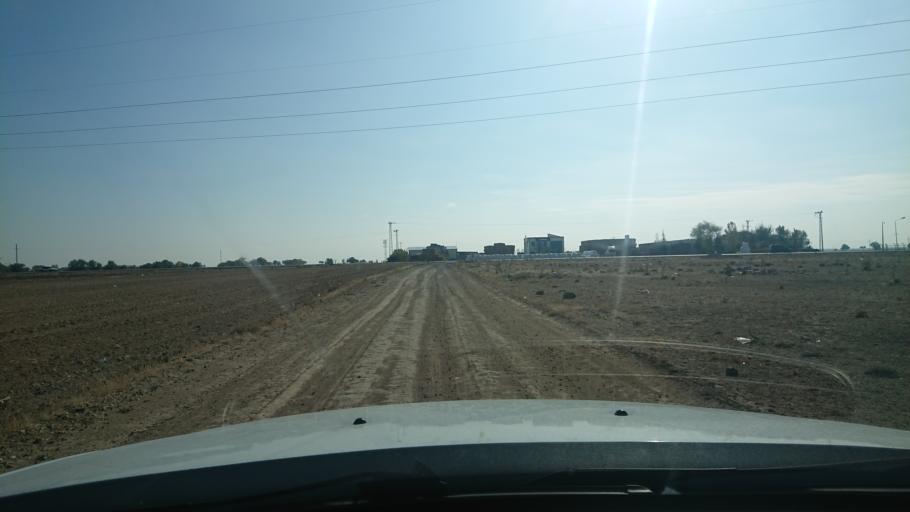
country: TR
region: Aksaray
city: Sultanhani
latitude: 38.2533
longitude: 33.4721
